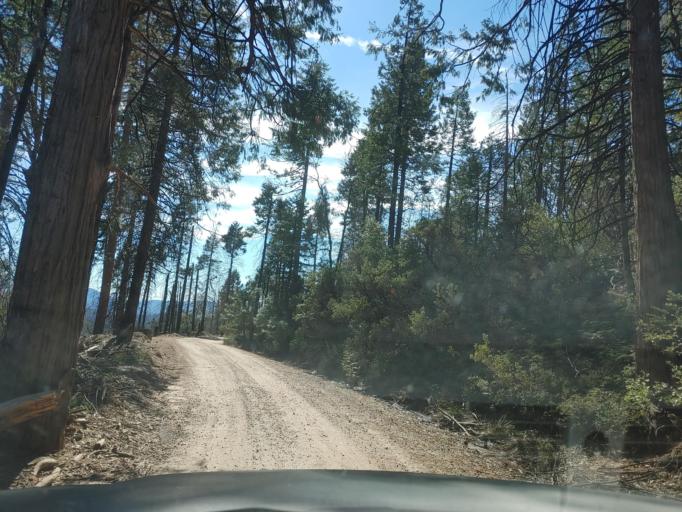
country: US
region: California
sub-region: Madera County
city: Ahwahnee
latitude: 37.4408
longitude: -119.6554
